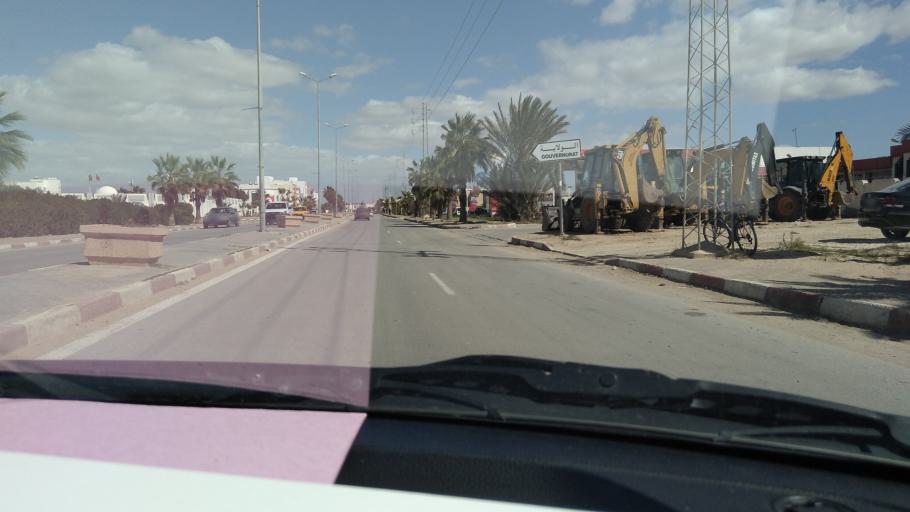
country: TN
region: Al Qayrawan
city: Kairouan
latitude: 35.6892
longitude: 10.1014
